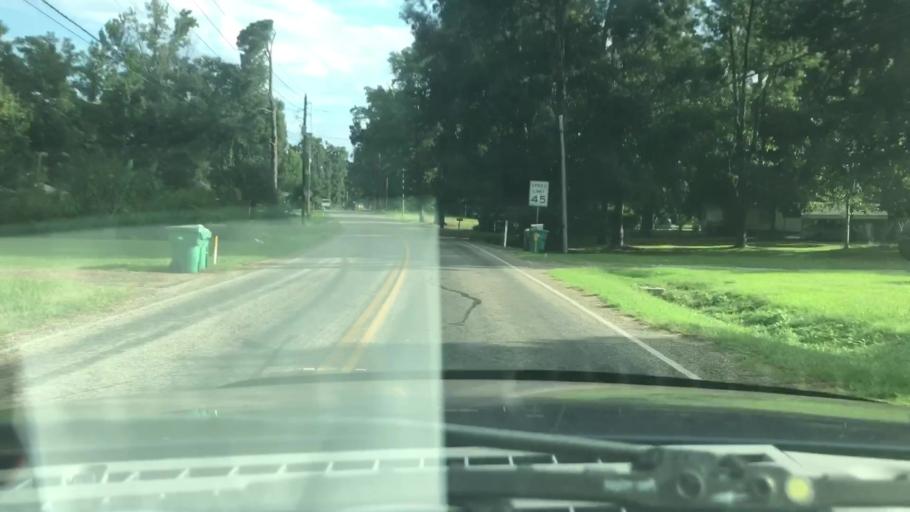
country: US
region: Texas
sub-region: Bowie County
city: Texarkana
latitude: 33.4023
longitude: -94.0649
